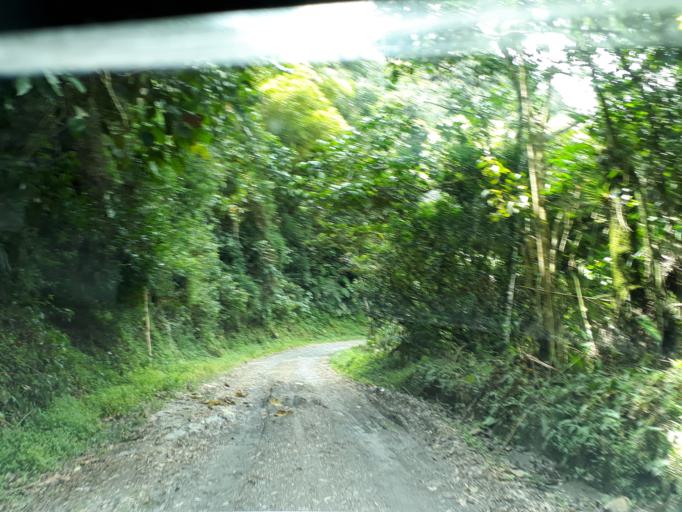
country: CO
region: Cundinamarca
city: Topaipi
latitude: 5.3063
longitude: -74.1982
